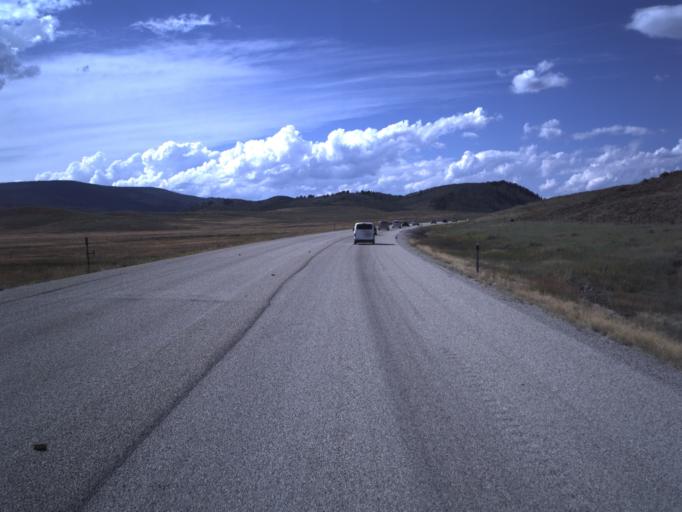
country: US
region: Utah
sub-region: Wasatch County
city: Heber
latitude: 40.2627
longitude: -111.2083
